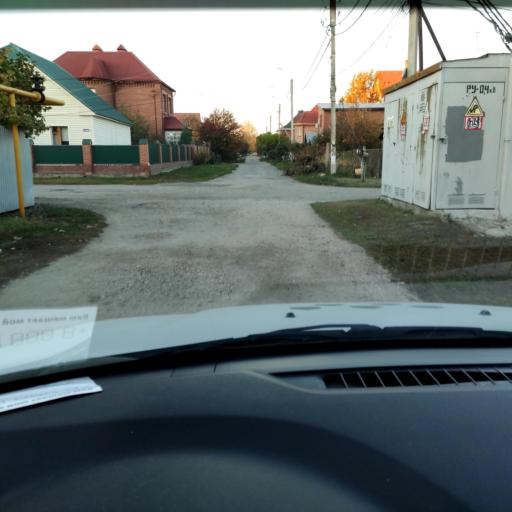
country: RU
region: Samara
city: Tol'yatti
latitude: 53.5104
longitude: 49.4014
